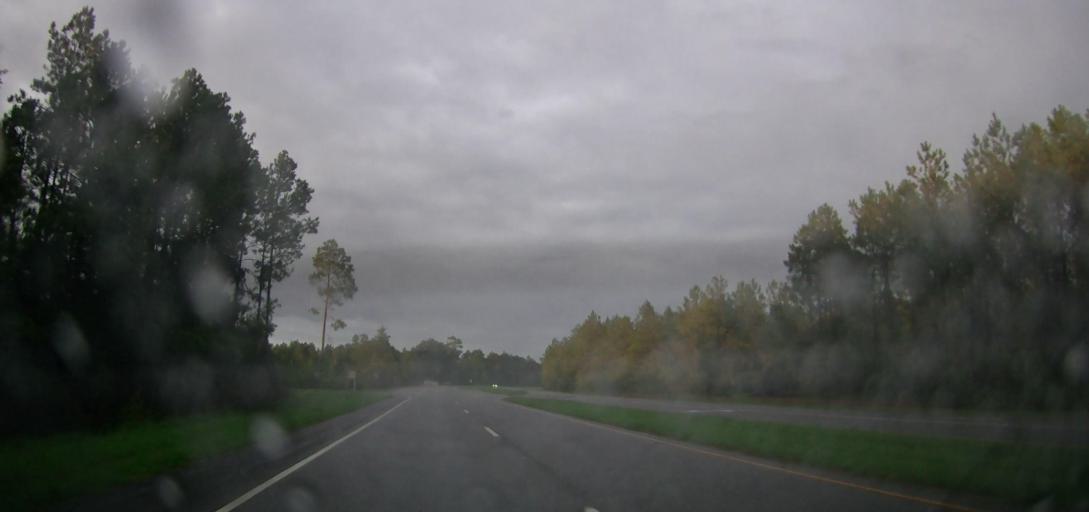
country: US
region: Georgia
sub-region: Clinch County
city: Homerville
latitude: 30.9982
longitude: -82.8639
